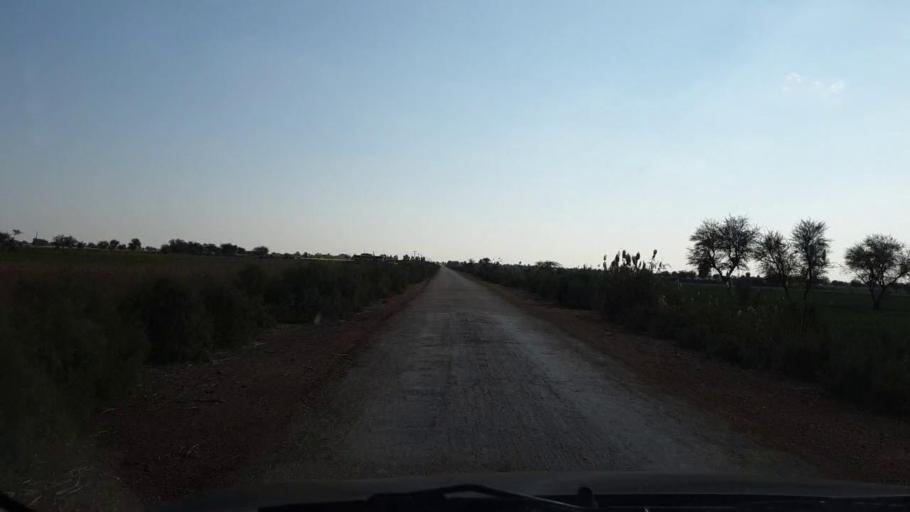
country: PK
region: Sindh
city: Sinjhoro
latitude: 26.0010
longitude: 68.8395
